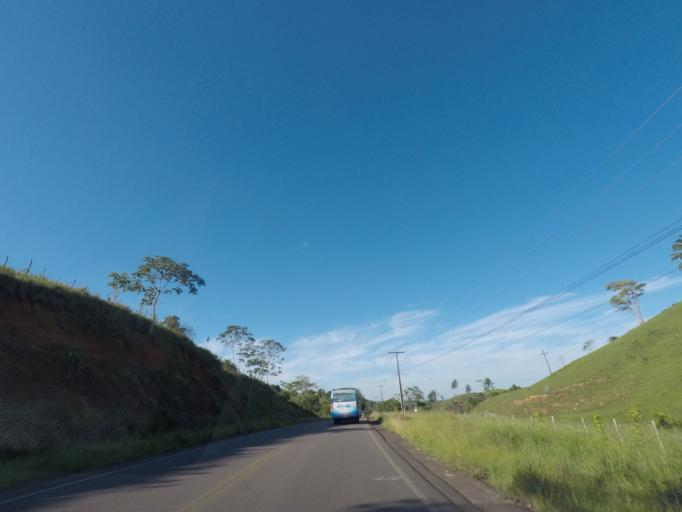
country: BR
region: Bahia
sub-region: Nazare
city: Nazare
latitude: -13.0492
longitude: -39.0071
